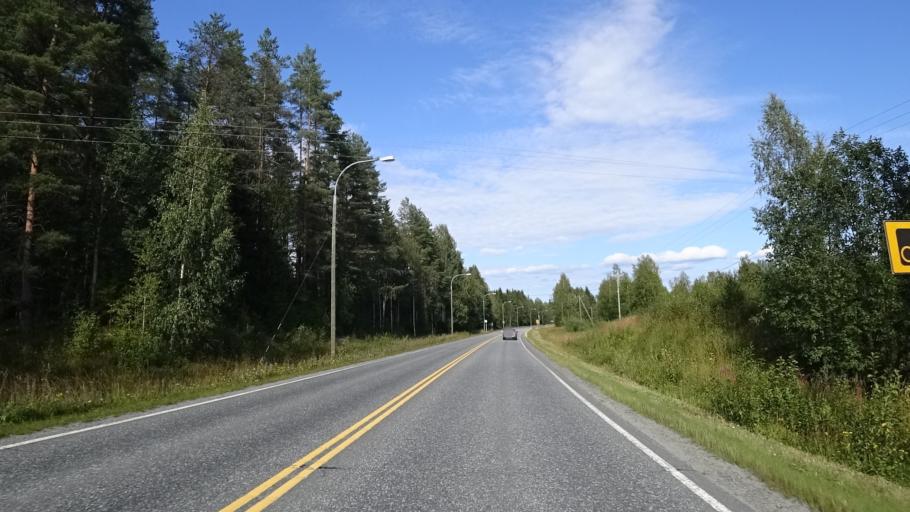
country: FI
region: North Karelia
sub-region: Joensuu
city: Eno
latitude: 62.7928
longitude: 30.0868
